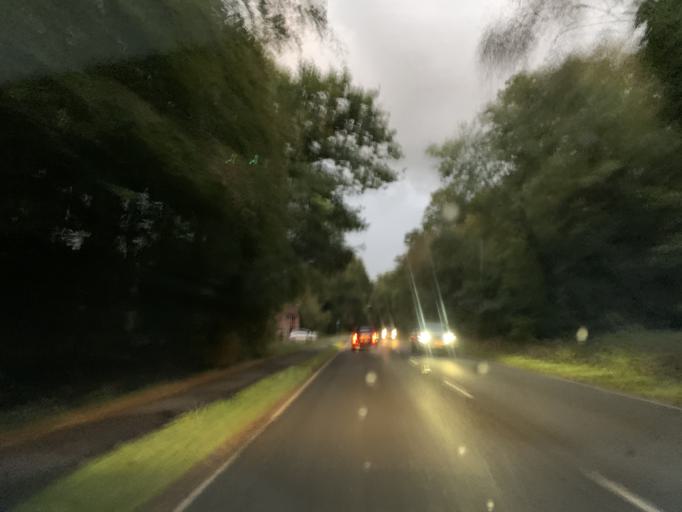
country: GB
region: England
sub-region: Hampshire
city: Lyndhurst
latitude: 50.8821
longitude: -1.5488
